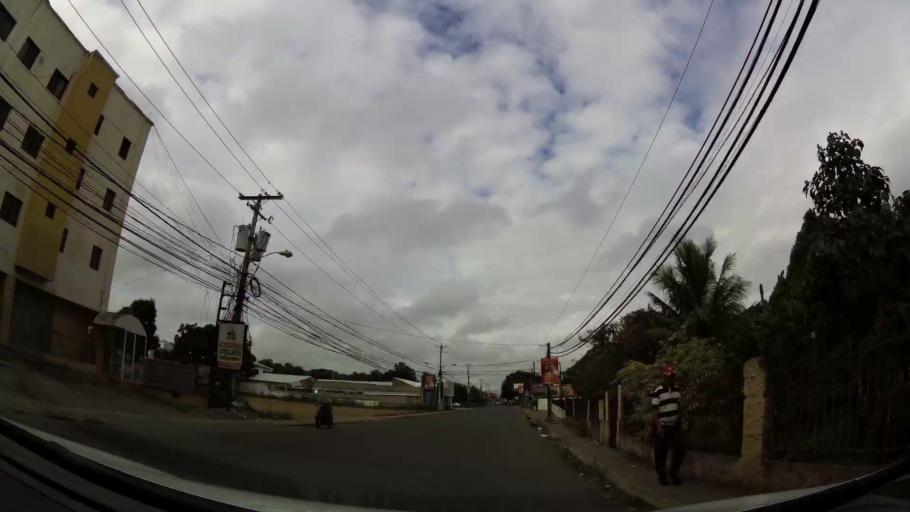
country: DO
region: Santiago
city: Santiago de los Caballeros
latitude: 19.4680
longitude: -70.6554
